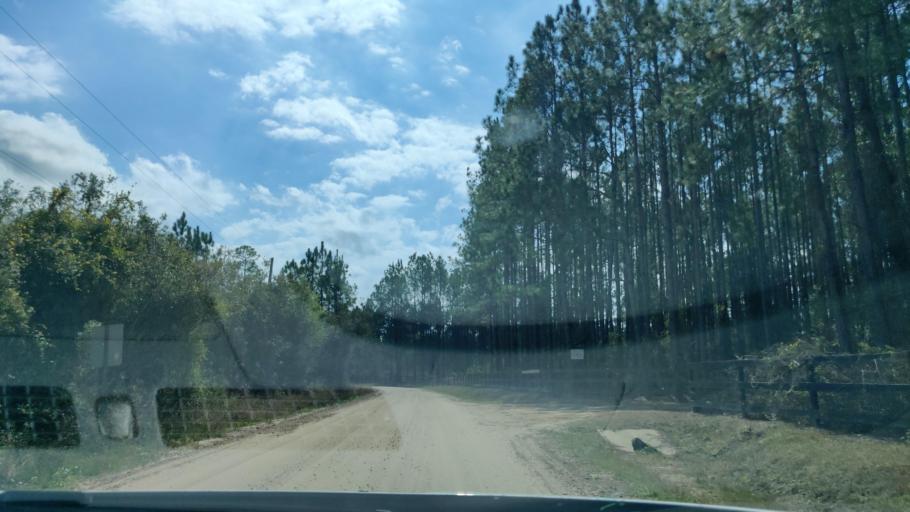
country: US
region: Florida
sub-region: Duval County
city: Baldwin
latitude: 30.1731
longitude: -81.9567
